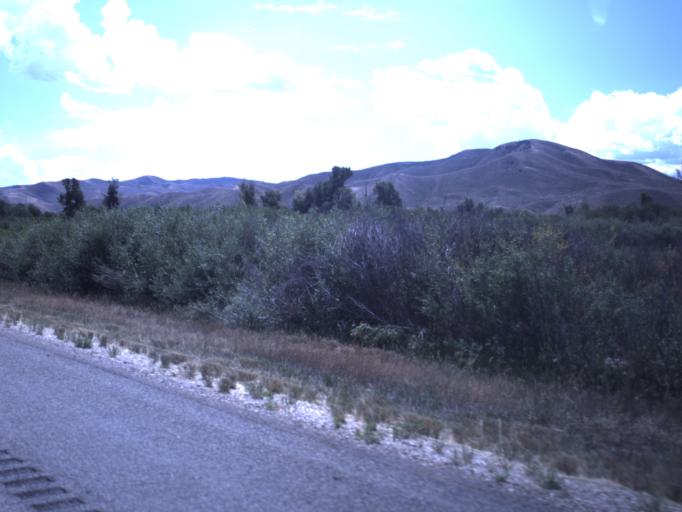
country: US
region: Utah
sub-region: Summit County
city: Coalville
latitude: 41.0346
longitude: -111.5084
